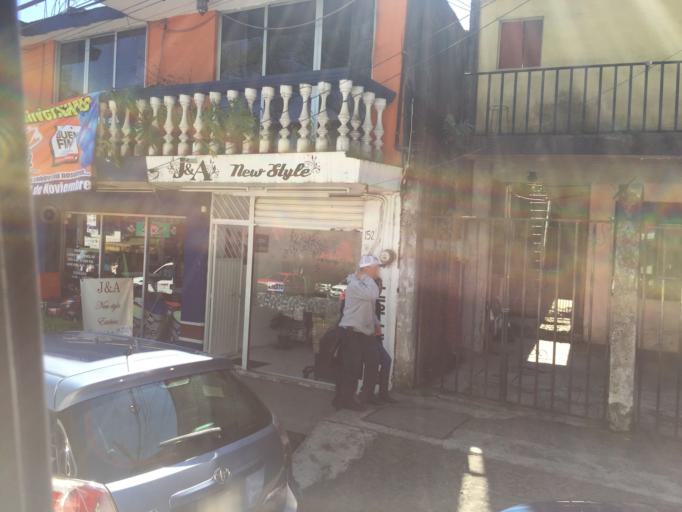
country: MX
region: Veracruz
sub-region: Xalapa
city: Xalapa de Enriquez
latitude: 19.5399
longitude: -96.9199
